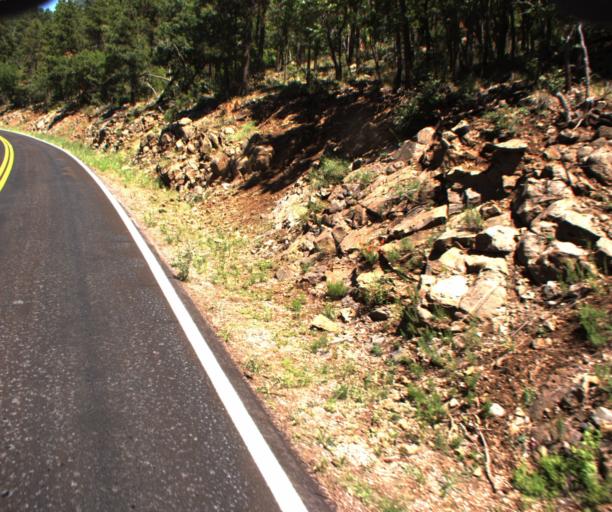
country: US
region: Arizona
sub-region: Greenlee County
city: Morenci
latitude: 33.4495
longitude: -109.3658
